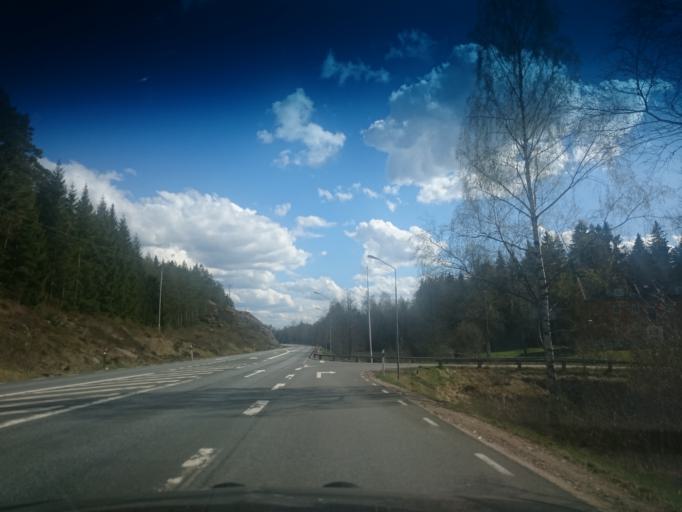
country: SE
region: Kronoberg
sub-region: Vaxjo Kommun
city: Braas
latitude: 57.2200
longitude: 15.1453
